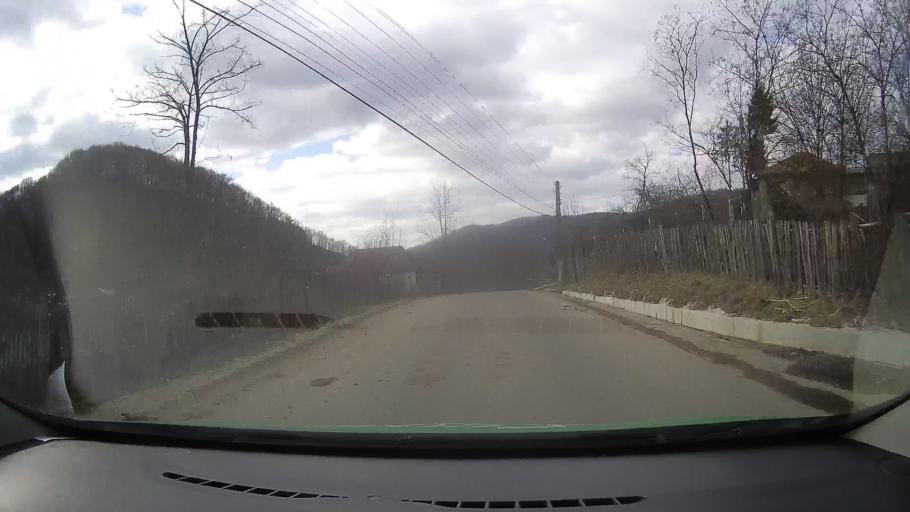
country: RO
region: Dambovita
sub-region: Comuna Visinesti
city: Visinesti
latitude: 45.1005
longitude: 25.5796
